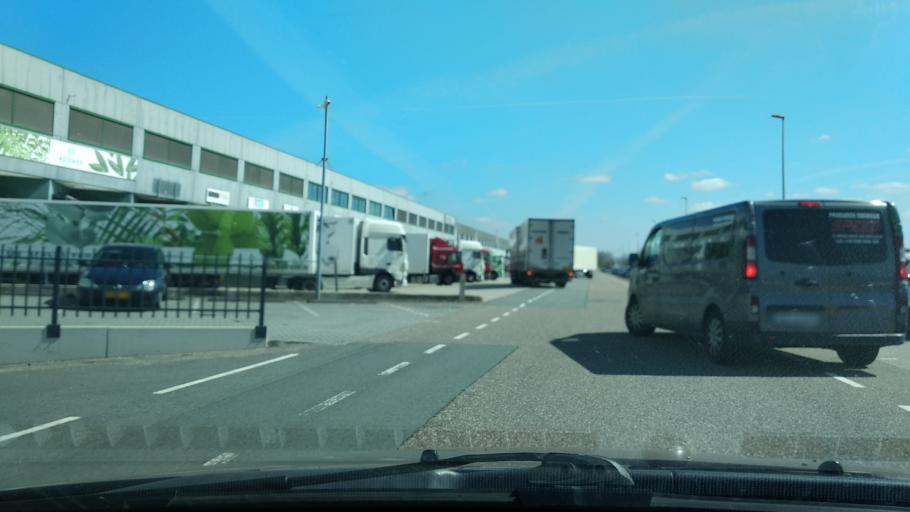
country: NL
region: South Holland
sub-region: Gemeente Westland
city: Honselersdijk
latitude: 51.9969
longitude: 4.2337
